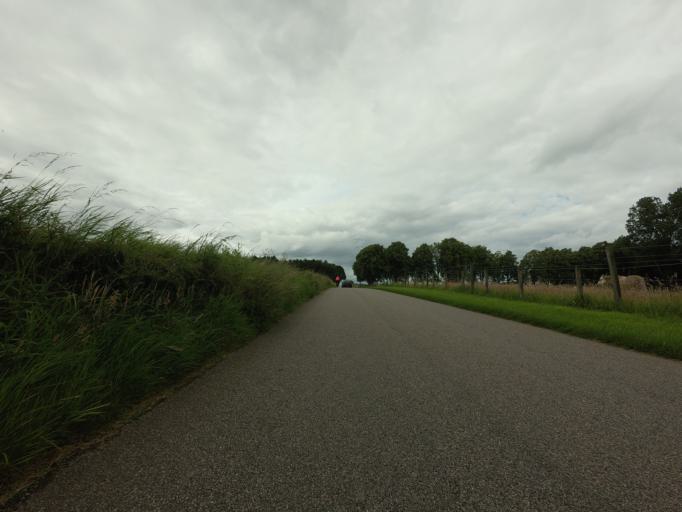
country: GB
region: Scotland
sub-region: Moray
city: Forres
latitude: 57.6007
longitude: -3.7222
